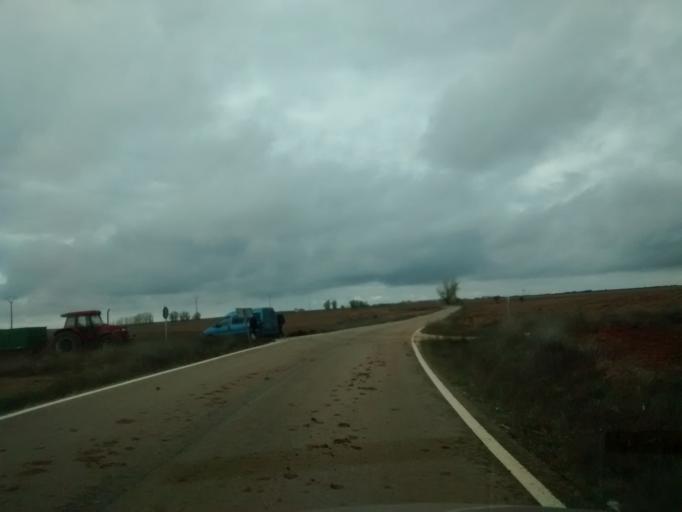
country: ES
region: Aragon
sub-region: Provincia de Zaragoza
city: Torralba de los Frailes
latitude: 41.0432
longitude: -1.6370
